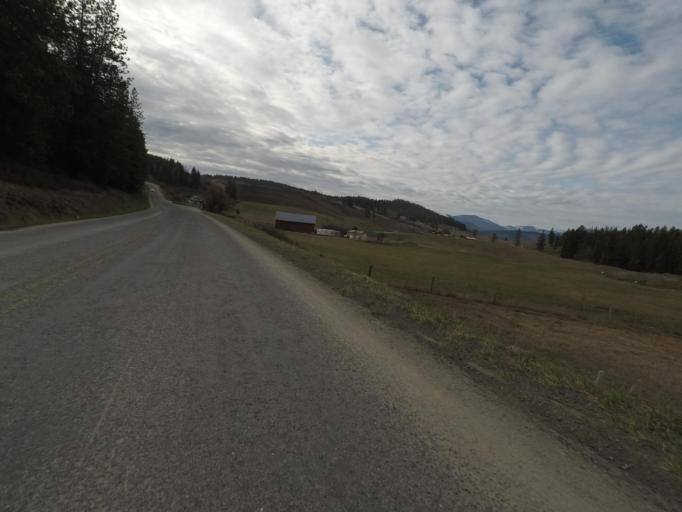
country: US
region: Washington
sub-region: Stevens County
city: Colville
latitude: 48.5223
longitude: -117.8811
